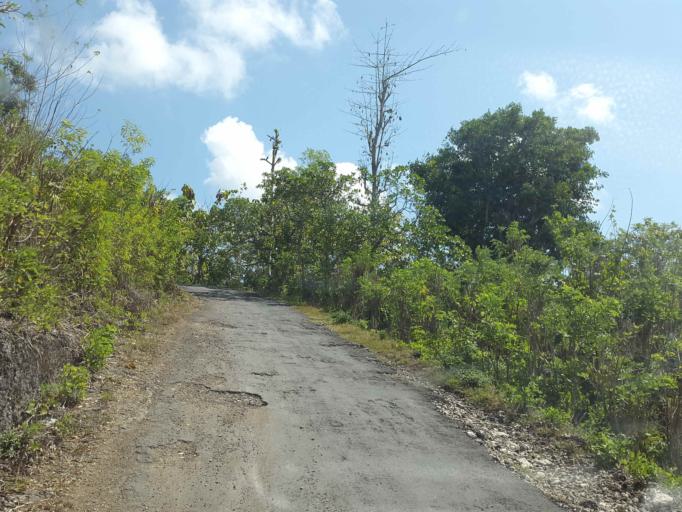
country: ID
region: Bali
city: Pondokkaha Kelod
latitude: -8.7288
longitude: 115.5009
